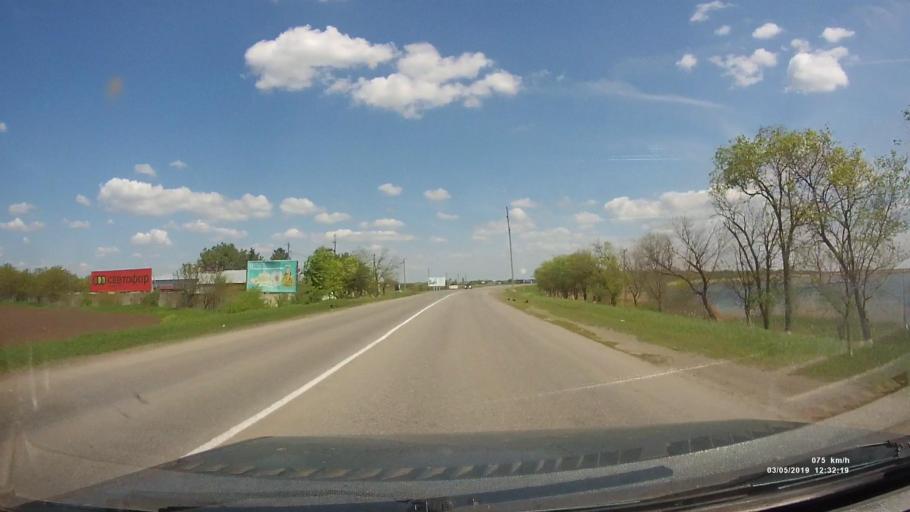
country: RU
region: Rostov
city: Semikarakorsk
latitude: 47.5108
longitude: 40.7576
